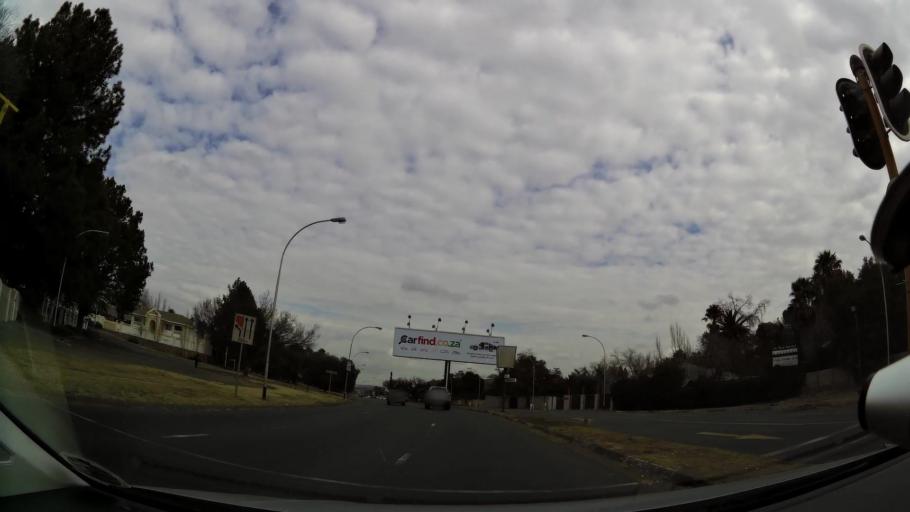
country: ZA
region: Orange Free State
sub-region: Mangaung Metropolitan Municipality
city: Bloemfontein
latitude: -29.0985
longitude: 26.2232
